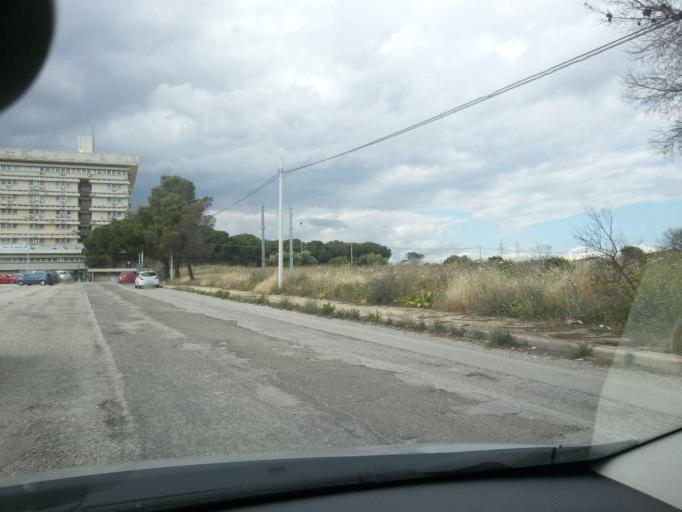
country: IT
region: Apulia
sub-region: Provincia di Taranto
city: Paolo VI
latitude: 40.5372
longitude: 17.2770
